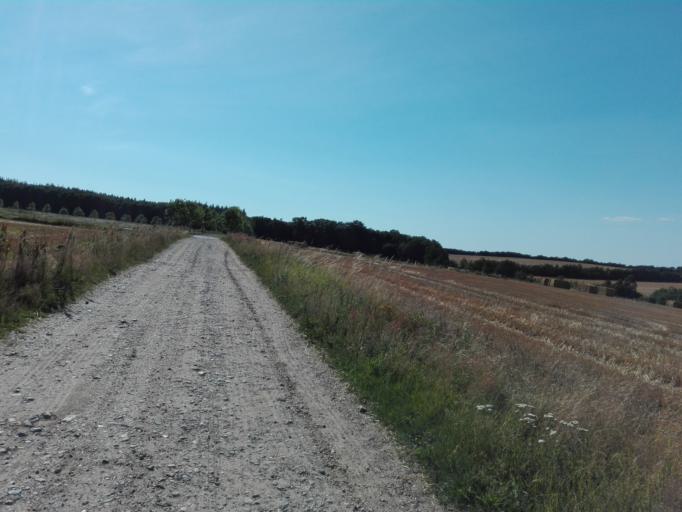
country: DK
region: Central Jutland
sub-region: Odder Kommune
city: Odder
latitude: 55.9566
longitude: 10.0764
